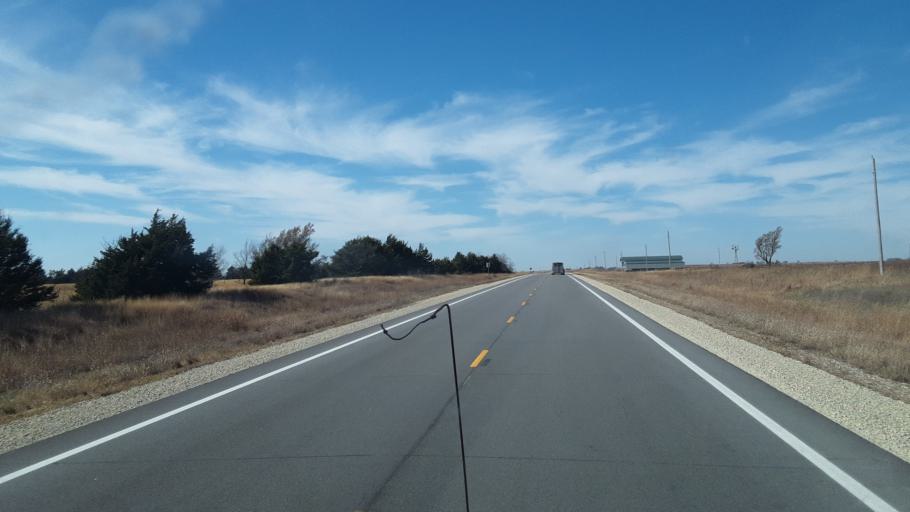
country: US
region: Kansas
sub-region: Marion County
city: Marion
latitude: 38.3629
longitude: -96.7966
